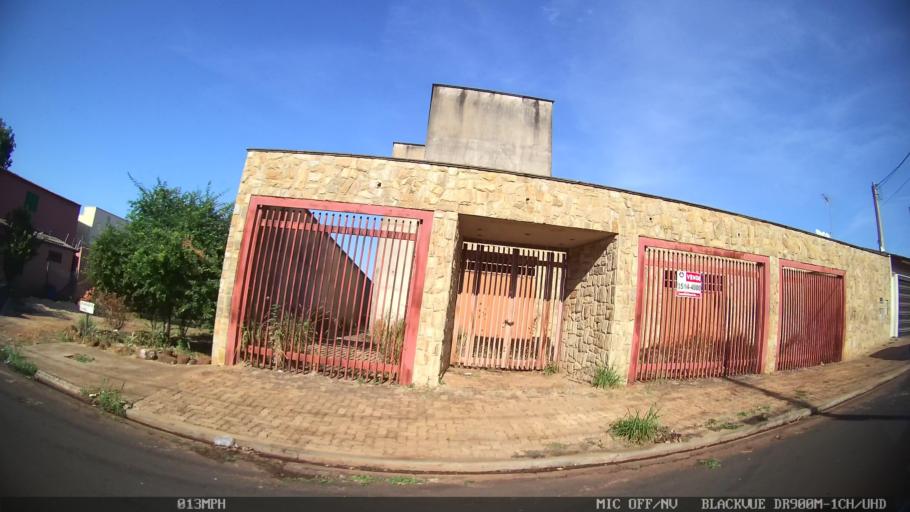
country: BR
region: Sao Paulo
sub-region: Ribeirao Preto
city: Ribeirao Preto
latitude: -21.1762
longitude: -47.7612
